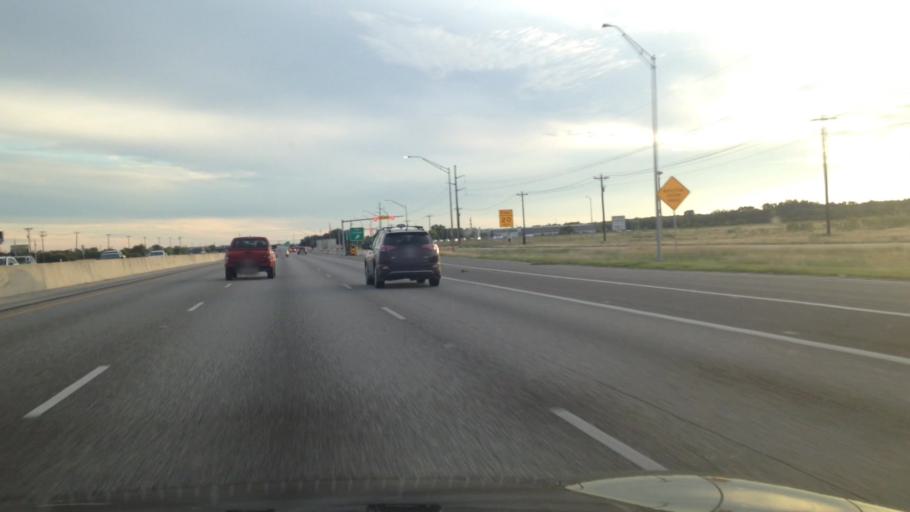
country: US
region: Texas
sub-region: Hays County
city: Kyle
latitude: 29.9260
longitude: -97.8913
